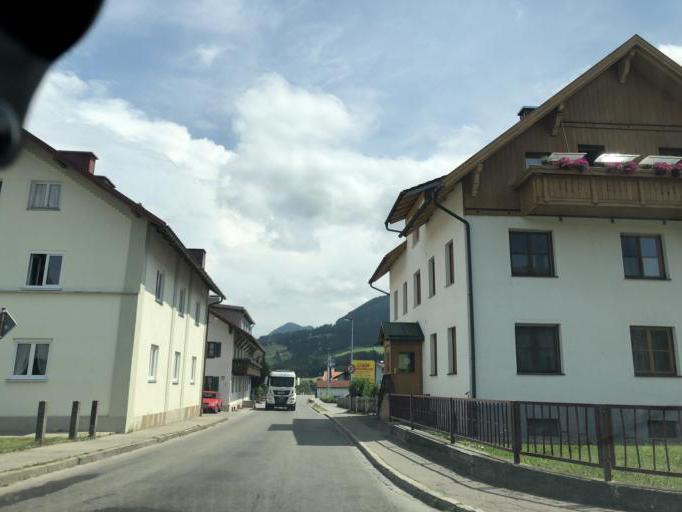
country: DE
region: Bavaria
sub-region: Swabia
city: Wertach
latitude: 47.6024
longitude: 10.4124
